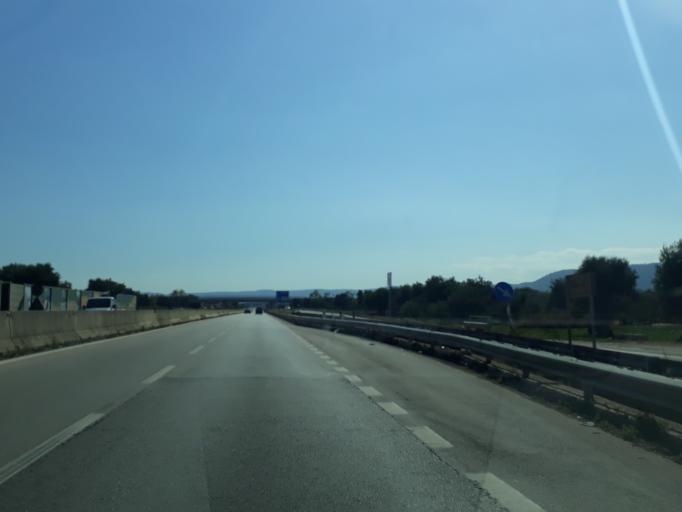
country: IT
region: Apulia
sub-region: Provincia di Brindisi
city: Fasano
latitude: 40.8763
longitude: 17.3403
